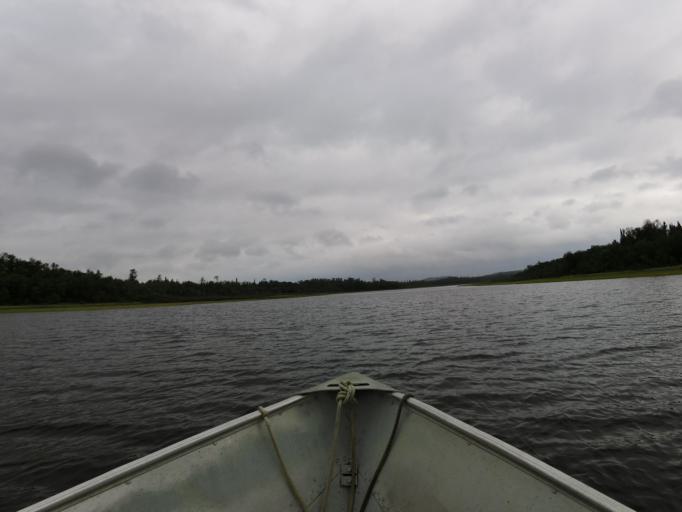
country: CA
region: Ontario
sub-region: Rainy River District
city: Atikokan
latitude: 49.5962
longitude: -91.3550
